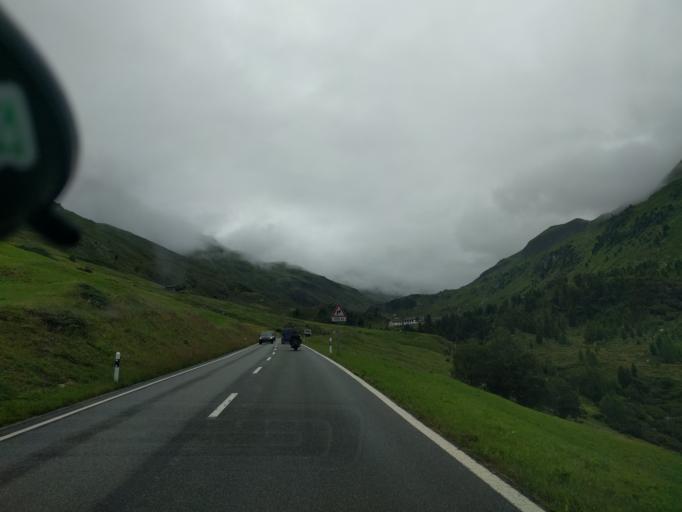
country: CH
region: Grisons
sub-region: Praettigau/Davos District
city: Davos
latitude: 46.7923
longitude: 9.9134
